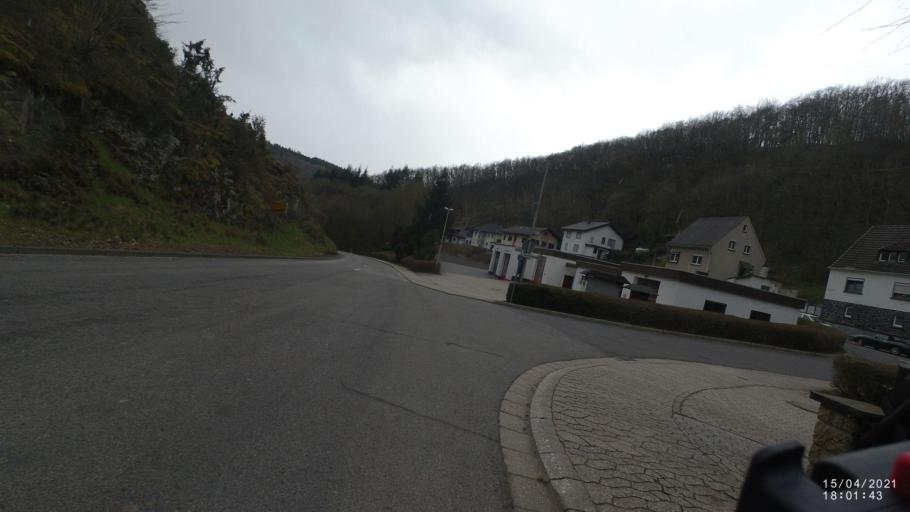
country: DE
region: Rheinland-Pfalz
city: Volkesfeld
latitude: 50.3884
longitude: 7.1499
